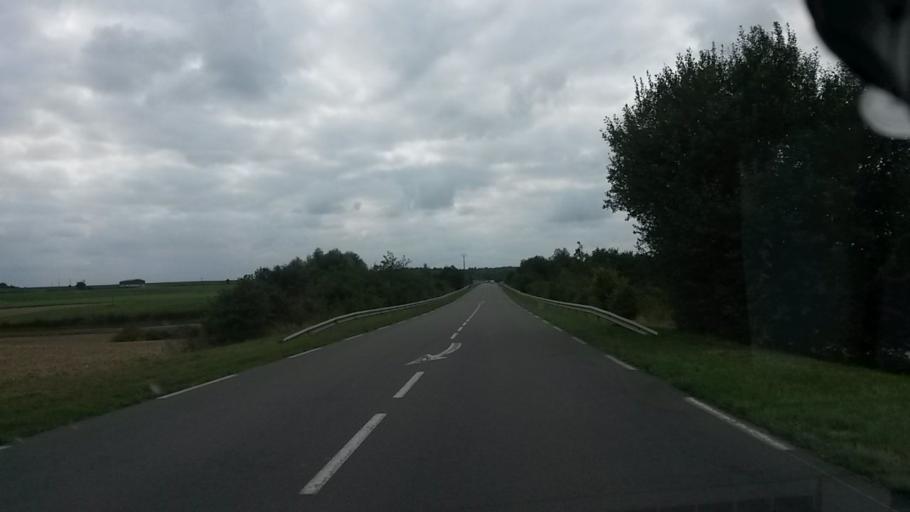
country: FR
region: Picardie
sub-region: Departement de la Somme
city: Corbie
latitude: 49.9459
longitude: 2.4271
